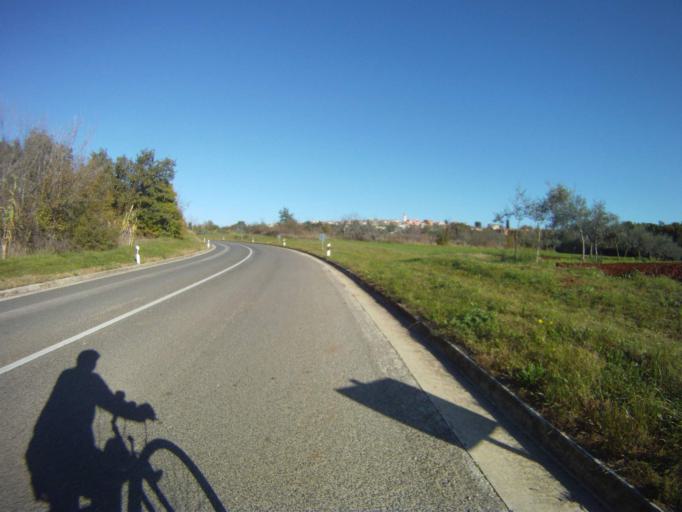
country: HR
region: Istarska
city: Buje
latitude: 45.3738
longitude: 13.6232
